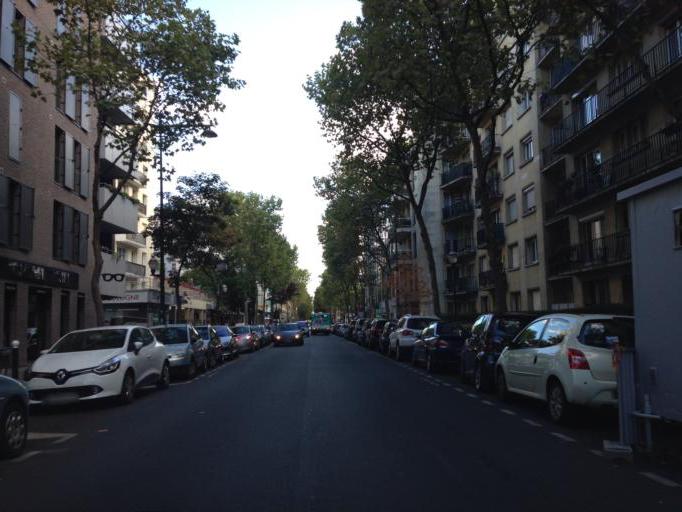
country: FR
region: Ile-de-France
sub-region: Departement des Hauts-de-Seine
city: Boulogne-Billancourt
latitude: 48.8300
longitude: 2.2456
